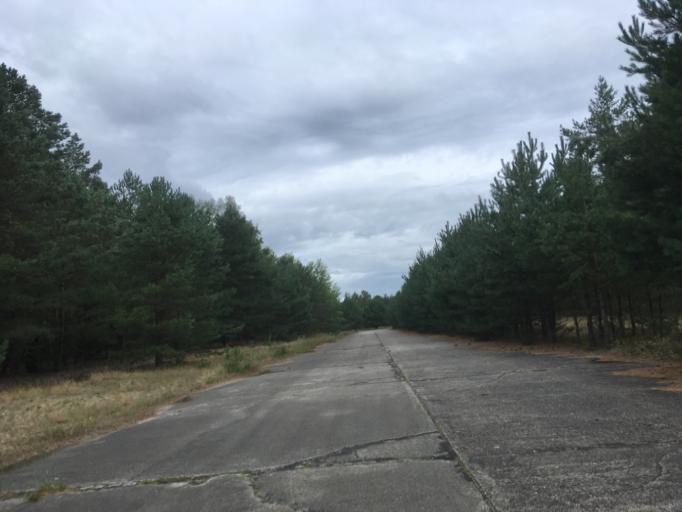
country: DE
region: Brandenburg
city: Halbe
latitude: 52.0376
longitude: 13.7624
